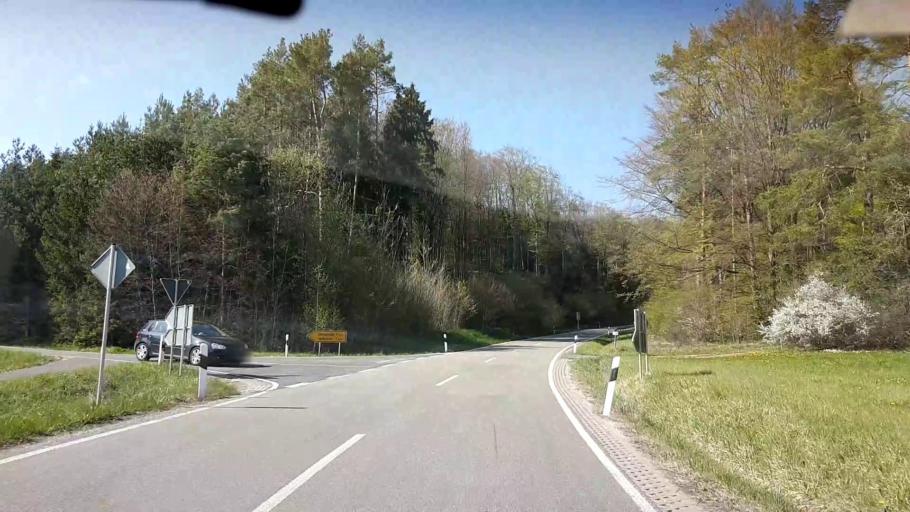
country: DE
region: Bavaria
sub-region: Upper Franconia
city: Pottenstein
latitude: 49.7926
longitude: 11.4123
